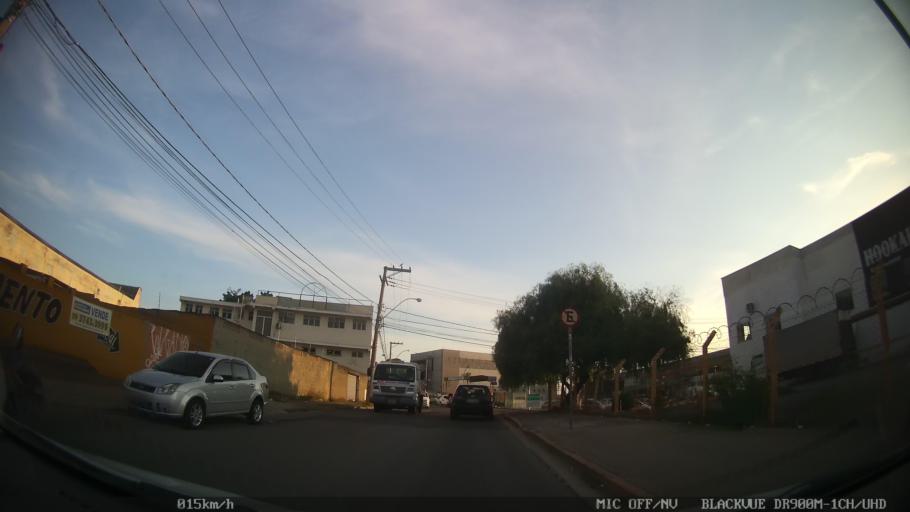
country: BR
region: Sao Paulo
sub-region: Campinas
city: Campinas
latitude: -22.9654
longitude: -47.1309
